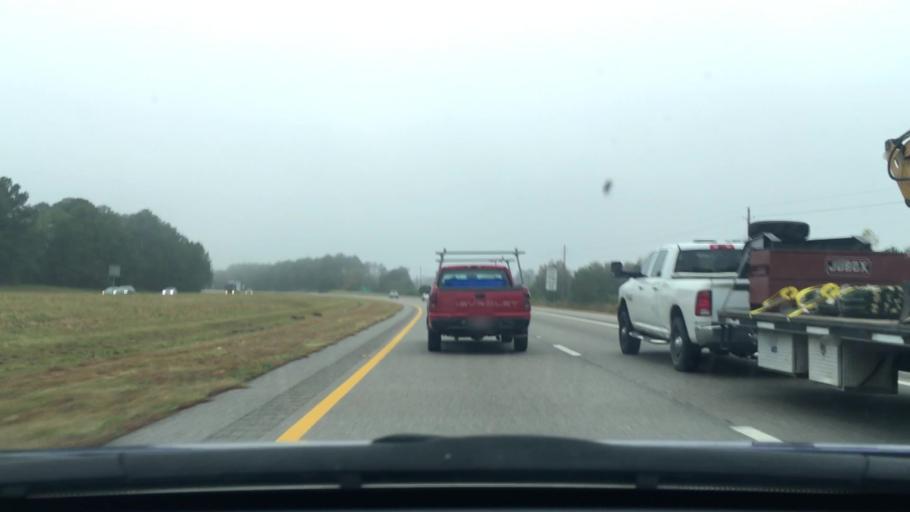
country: US
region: South Carolina
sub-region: Kershaw County
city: Camden
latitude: 34.2171
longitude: -80.5428
